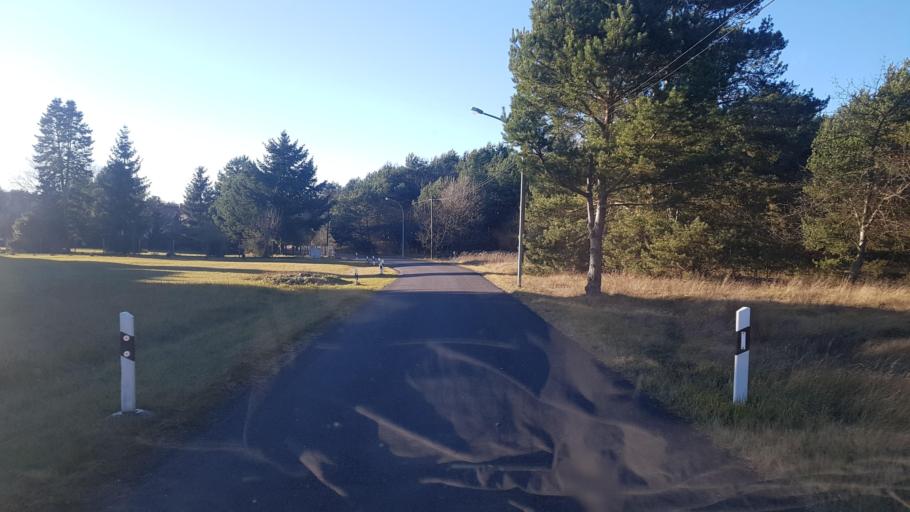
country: DE
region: Brandenburg
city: Tauer
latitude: 51.9356
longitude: 14.4659
